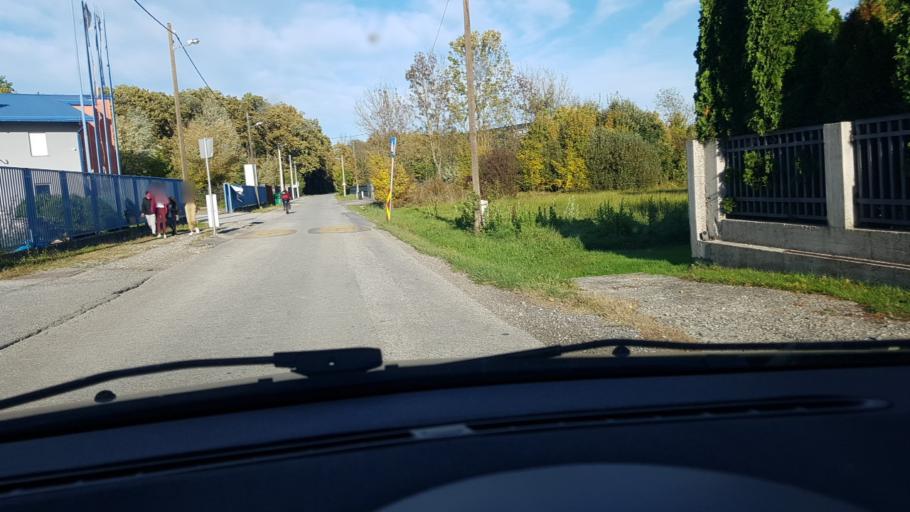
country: HR
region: Grad Zagreb
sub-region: Sesvete
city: Sesvete
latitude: 45.8009
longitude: 16.1529
